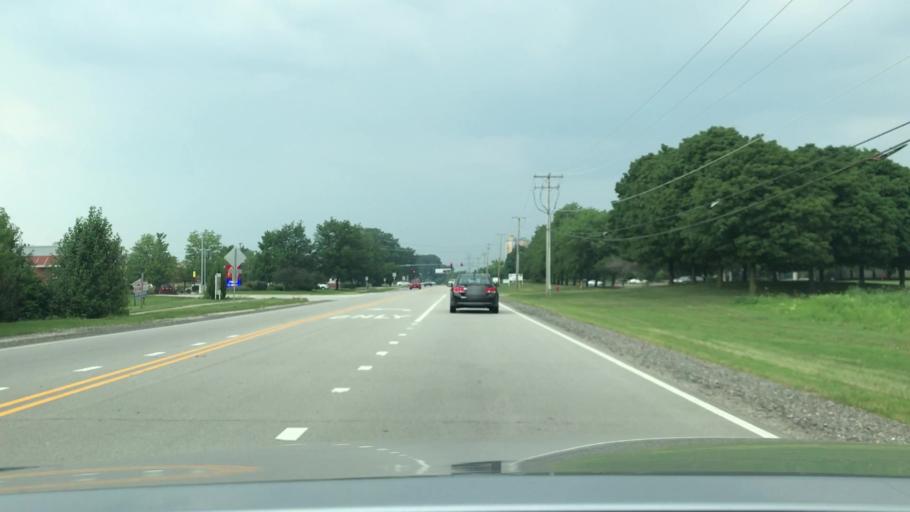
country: US
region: Illinois
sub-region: Will County
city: Plainfield
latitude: 41.6343
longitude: -88.2223
